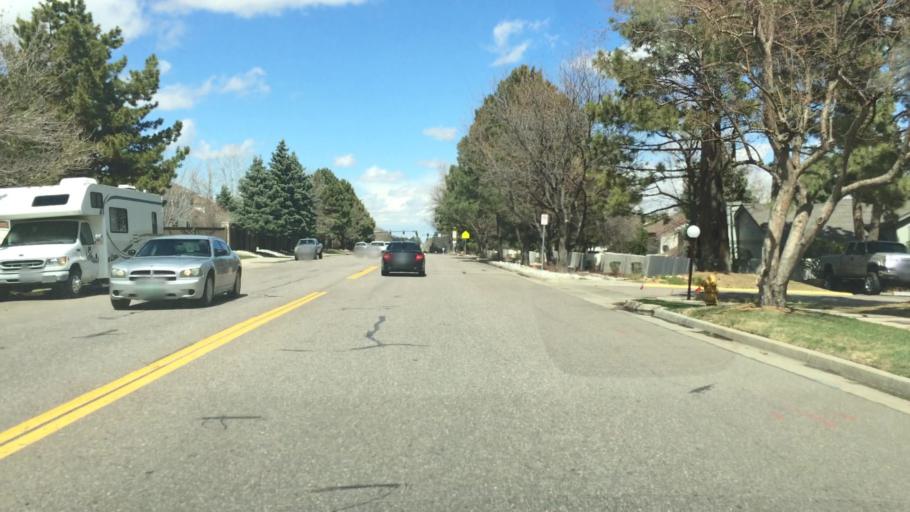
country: US
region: Colorado
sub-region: Arapahoe County
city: Centennial
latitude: 39.6001
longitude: -104.8761
